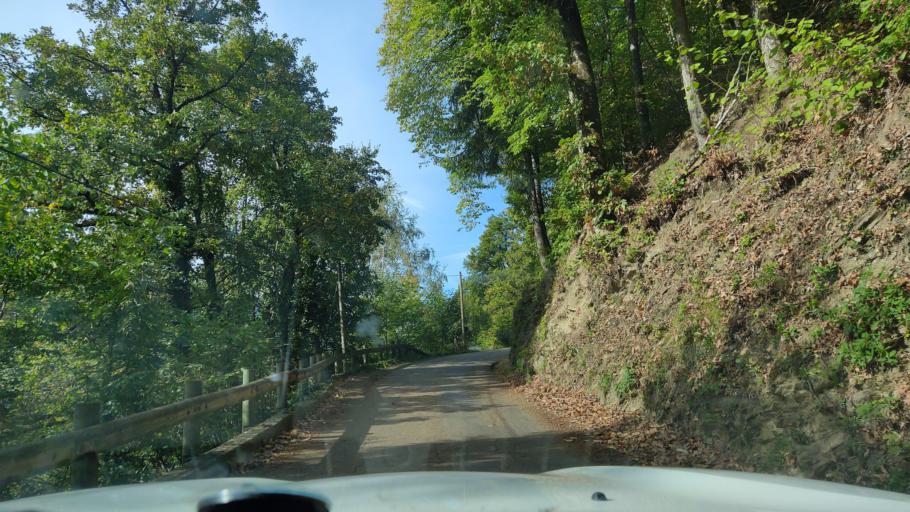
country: FR
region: Rhone-Alpes
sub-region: Departement de la Savoie
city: Beaufort
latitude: 45.7227
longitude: 6.5128
